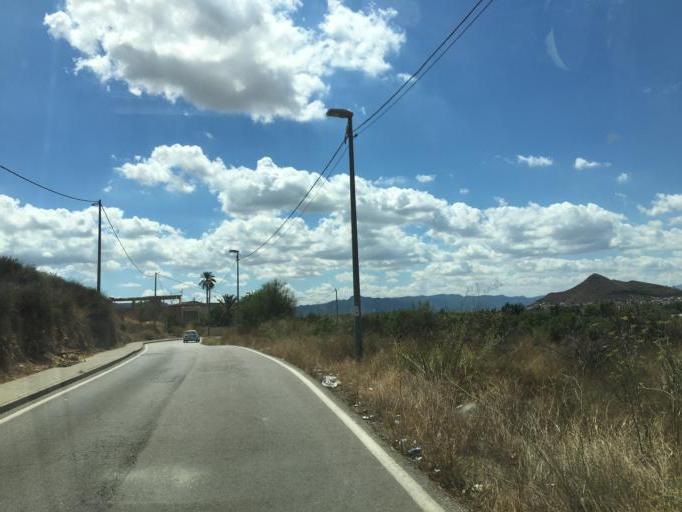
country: ES
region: Murcia
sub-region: Murcia
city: Santomera
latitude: 38.0529
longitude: -1.0679
